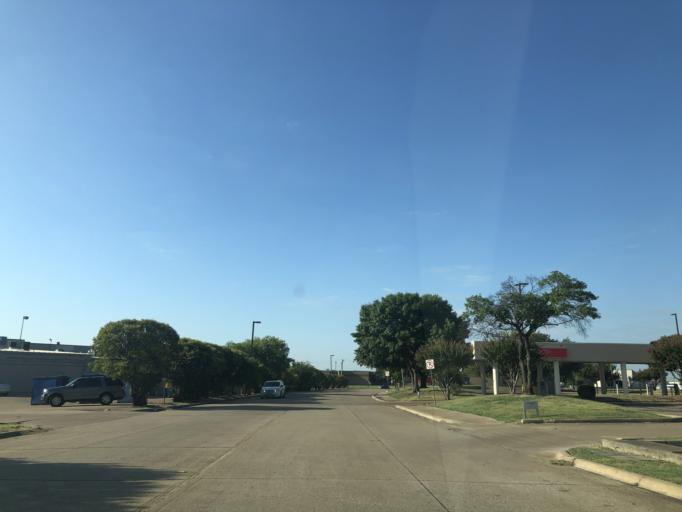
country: US
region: Texas
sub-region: Dallas County
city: Grand Prairie
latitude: 32.7401
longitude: -97.0176
